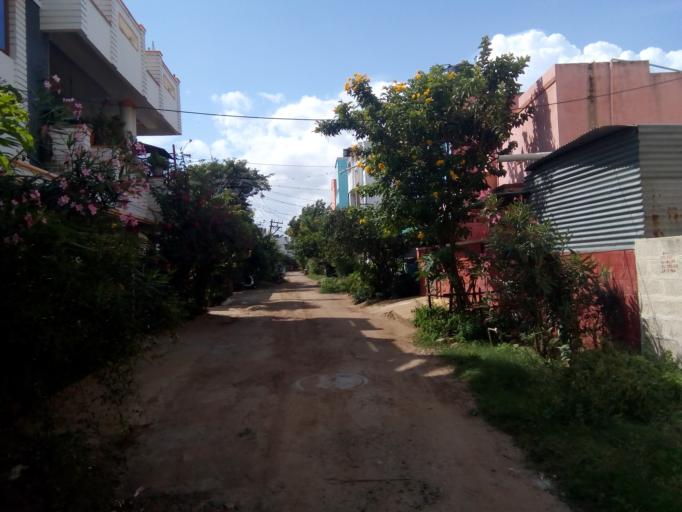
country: IN
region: Tamil Nadu
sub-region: Coimbatore
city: Singanallur
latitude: 10.9977
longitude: 77.0373
